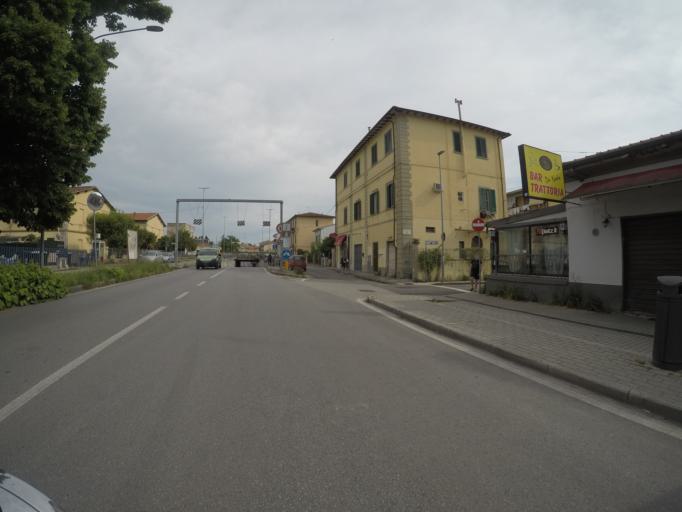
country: IT
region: Tuscany
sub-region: Province of Pisa
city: Madonna dell'Acqua
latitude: 43.7269
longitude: 10.3898
